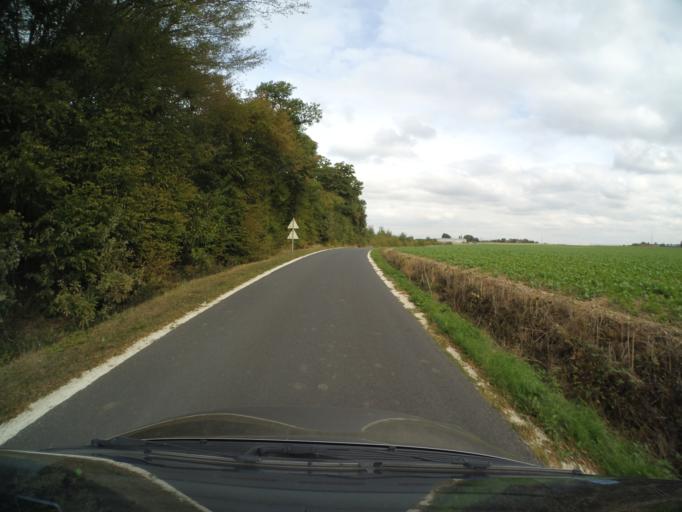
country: FR
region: Centre
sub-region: Departement d'Indre-et-Loire
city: Reugny
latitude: 47.4803
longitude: 0.8986
